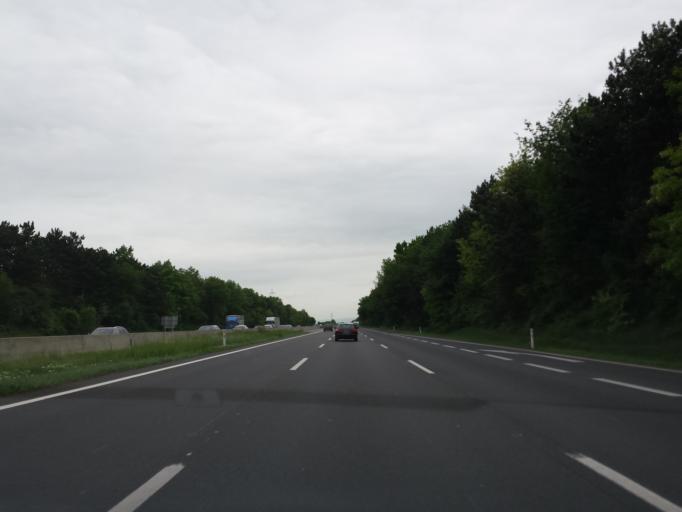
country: AT
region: Lower Austria
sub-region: Politischer Bezirk Baden
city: Leobersdorf
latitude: 47.9070
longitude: 16.2076
